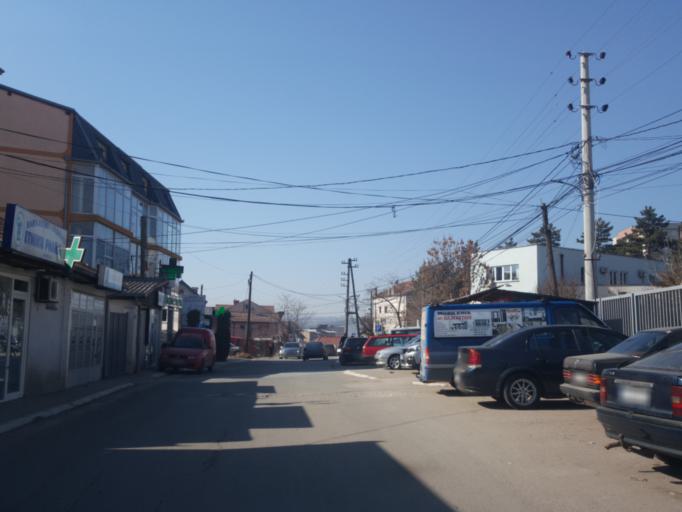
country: XK
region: Mitrovica
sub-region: Vushtrri
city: Vushtrri
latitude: 42.8244
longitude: 20.9651
